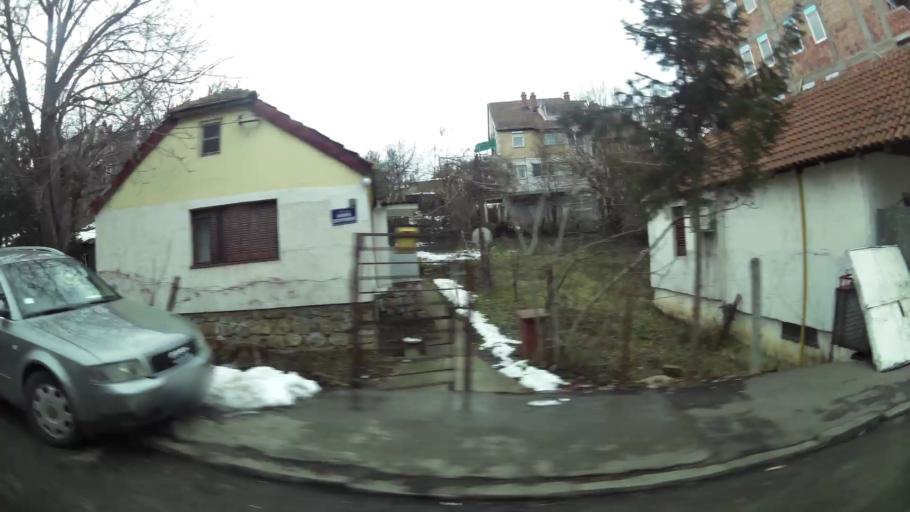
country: RS
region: Central Serbia
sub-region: Belgrade
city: Cukarica
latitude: 44.7646
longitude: 20.4091
